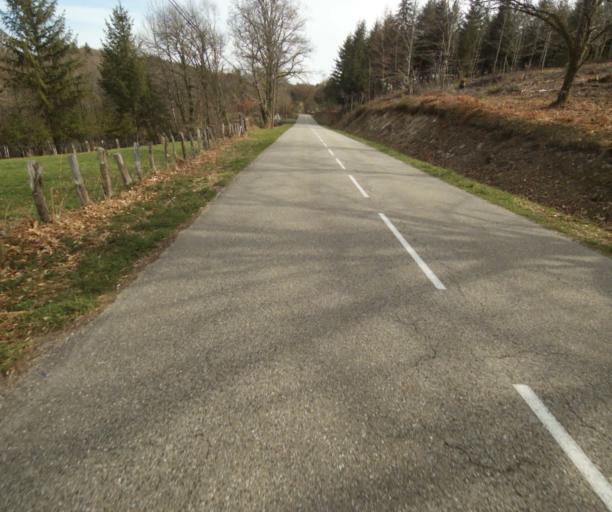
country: FR
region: Limousin
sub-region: Departement de la Correze
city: Correze
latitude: 45.4140
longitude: 1.8292
